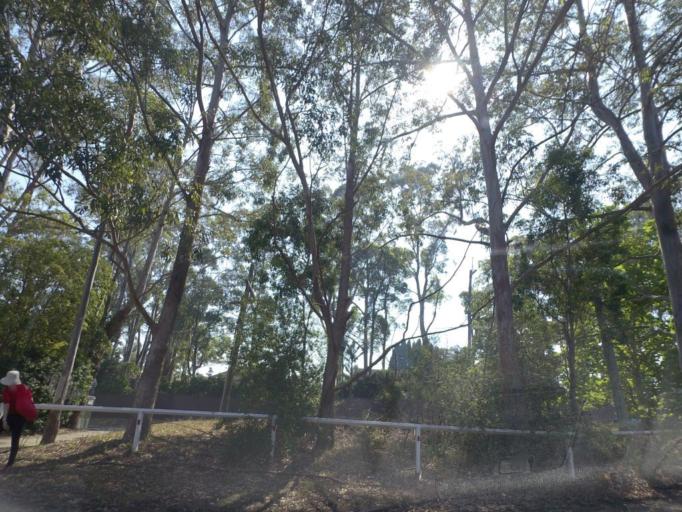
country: AU
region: New South Wales
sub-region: The Hills Shire
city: West Pennant
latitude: -33.7361
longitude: 151.0456
